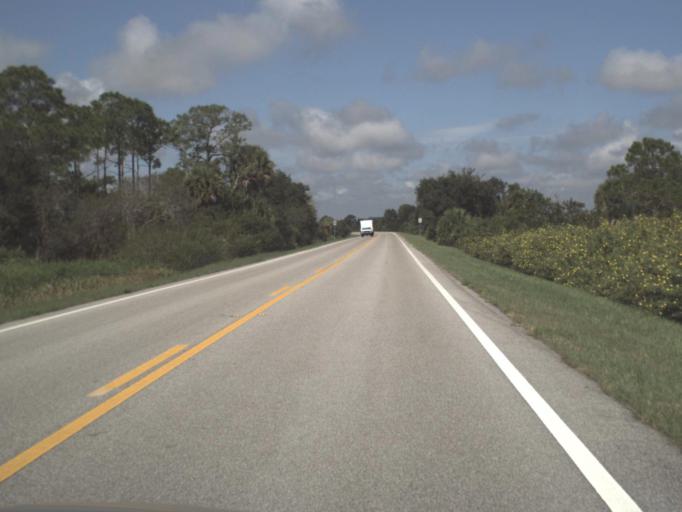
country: US
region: Florida
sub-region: Sarasota County
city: Warm Mineral Springs
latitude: 27.2142
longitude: -82.2651
